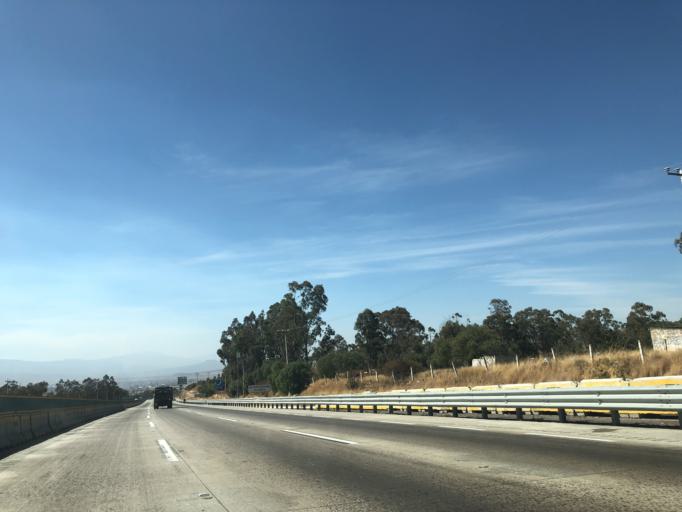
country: MX
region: Mexico
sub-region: Ixtapaluca
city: Jorge Jimenez Cantu
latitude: 19.3113
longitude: -98.8276
